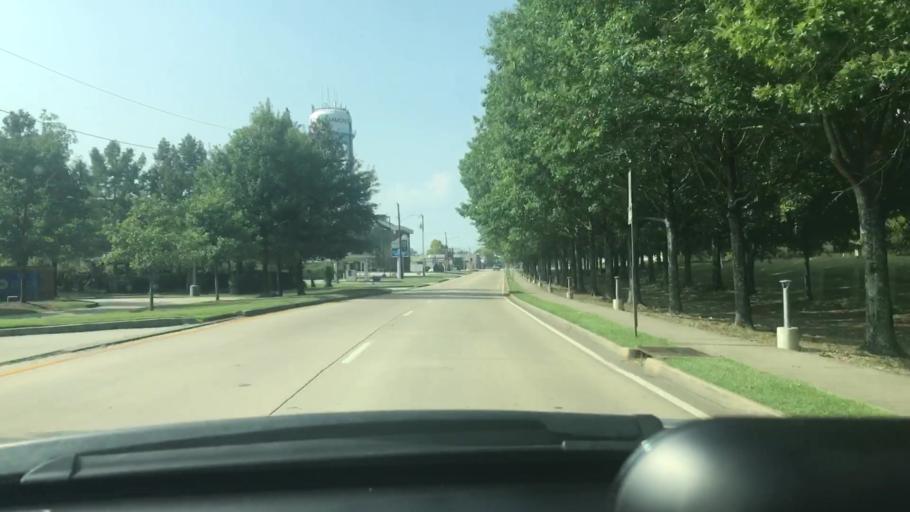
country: US
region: Louisiana
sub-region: Tangipahoa Parish
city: Hammond
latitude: 30.4984
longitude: -90.4597
